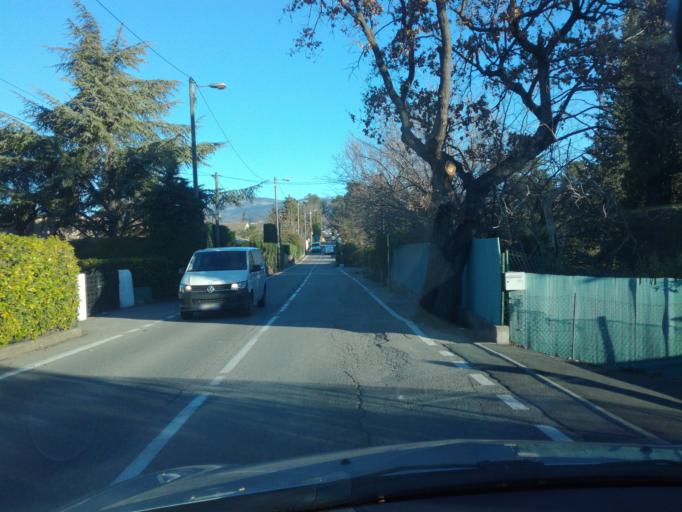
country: FR
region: Provence-Alpes-Cote d'Azur
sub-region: Departement des Alpes-Maritimes
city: La Roquette-sur-Siagne
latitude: 43.6084
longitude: 6.9674
